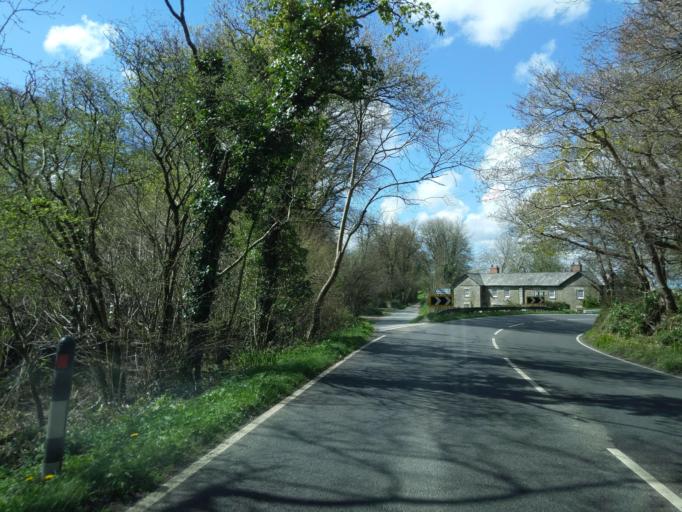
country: GB
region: England
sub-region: Cornwall
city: Bodmin
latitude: 50.4977
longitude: -4.7747
